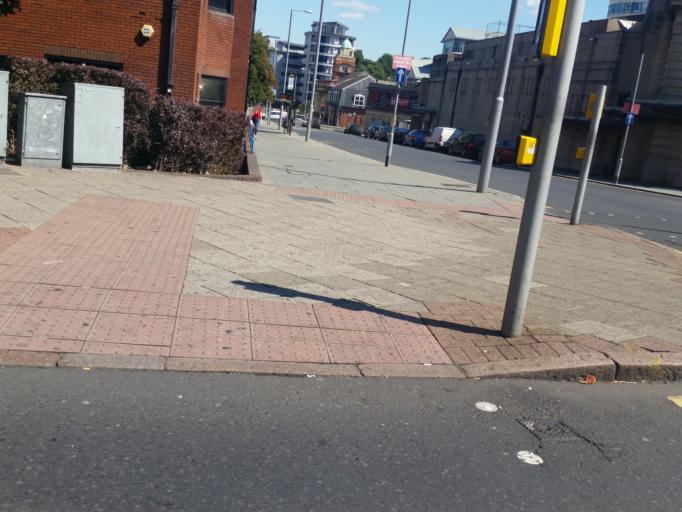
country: GB
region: England
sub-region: Nottingham
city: Nottingham
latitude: 52.9554
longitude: -1.1449
